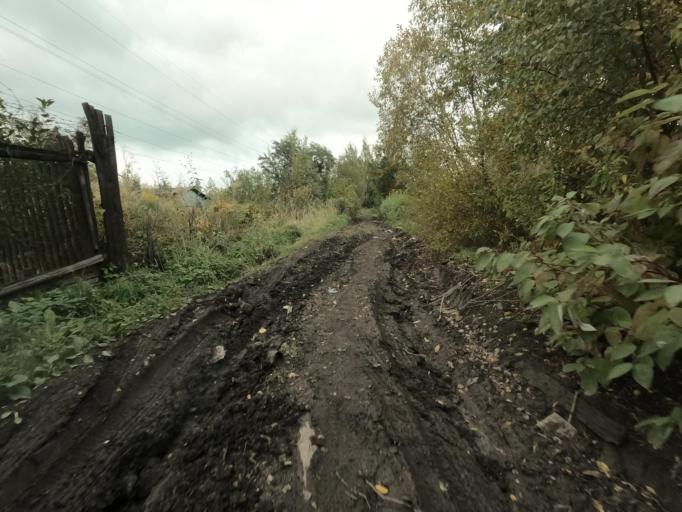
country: RU
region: St.-Petersburg
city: Pontonnyy
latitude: 59.7790
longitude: 30.6376
